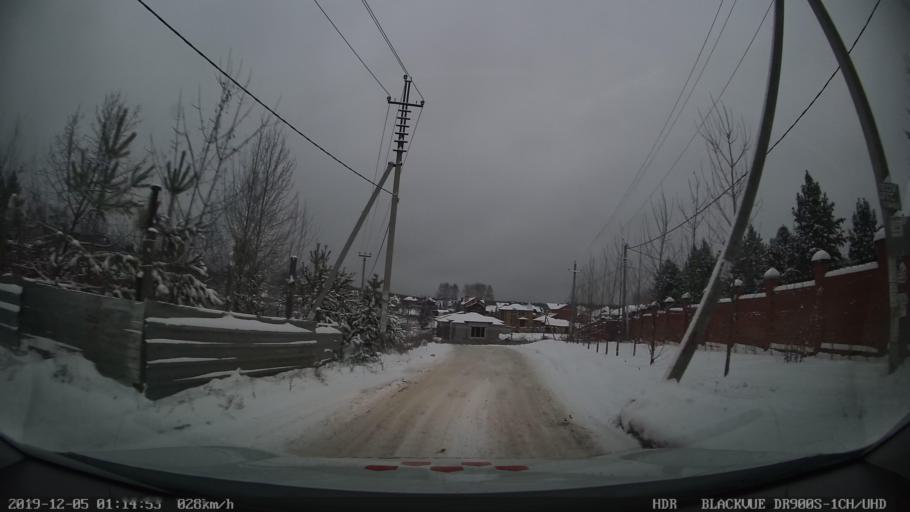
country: RU
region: Tatarstan
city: Stolbishchi
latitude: 55.6440
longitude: 49.1141
